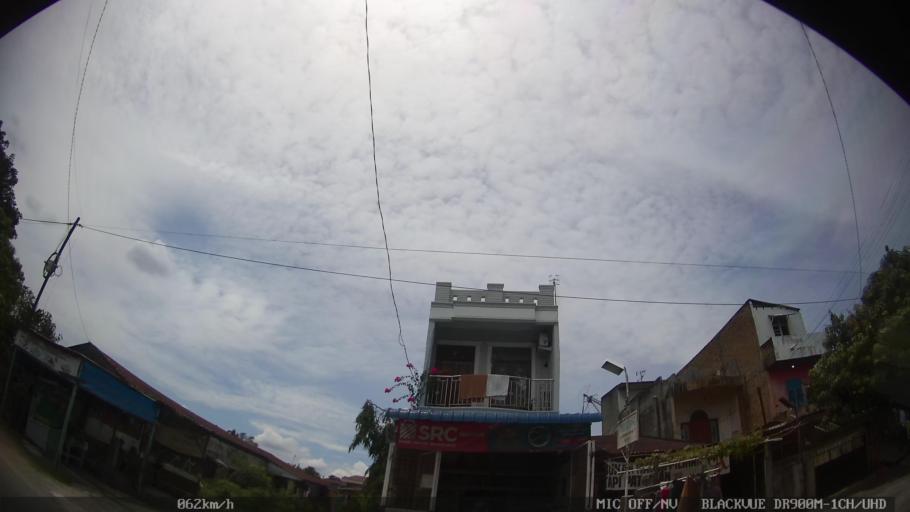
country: ID
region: North Sumatra
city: Sunggal
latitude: 3.5551
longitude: 98.6425
